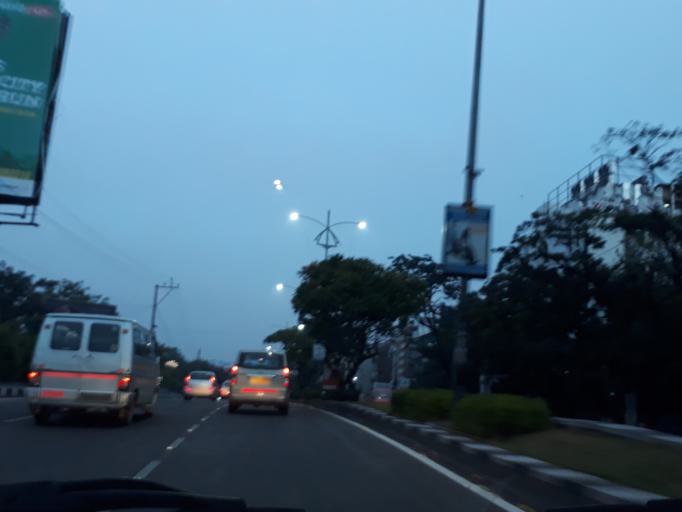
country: IN
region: Telangana
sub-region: Hyderabad
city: Hyderabad
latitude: 17.4240
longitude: 78.4237
